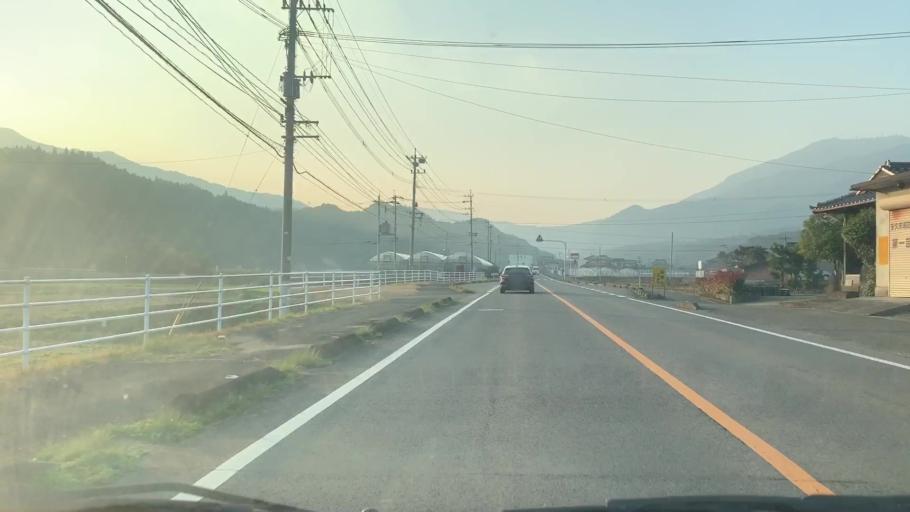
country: JP
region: Saga Prefecture
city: Takeocho-takeo
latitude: 33.2595
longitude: 130.0655
